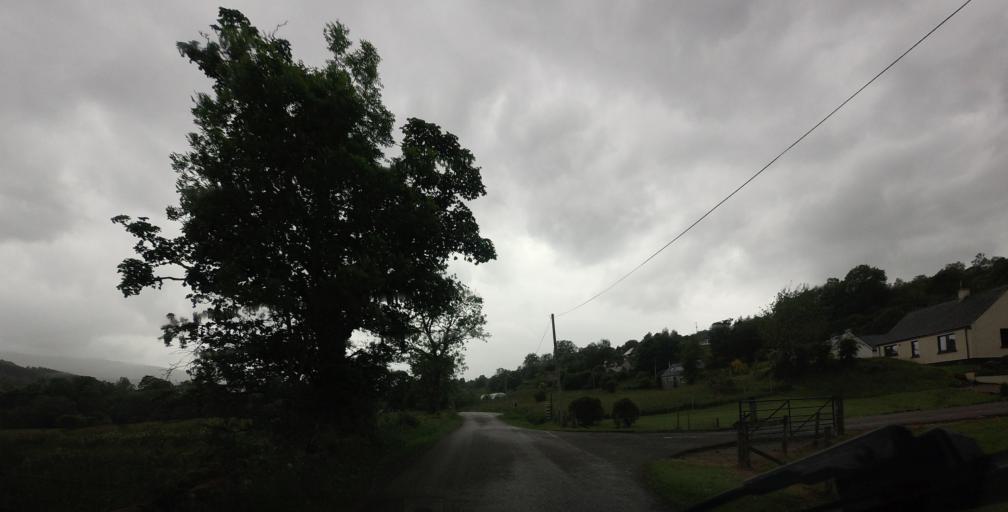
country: GB
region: Scotland
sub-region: Argyll and Bute
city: Oban
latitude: 56.7050
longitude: -5.5694
